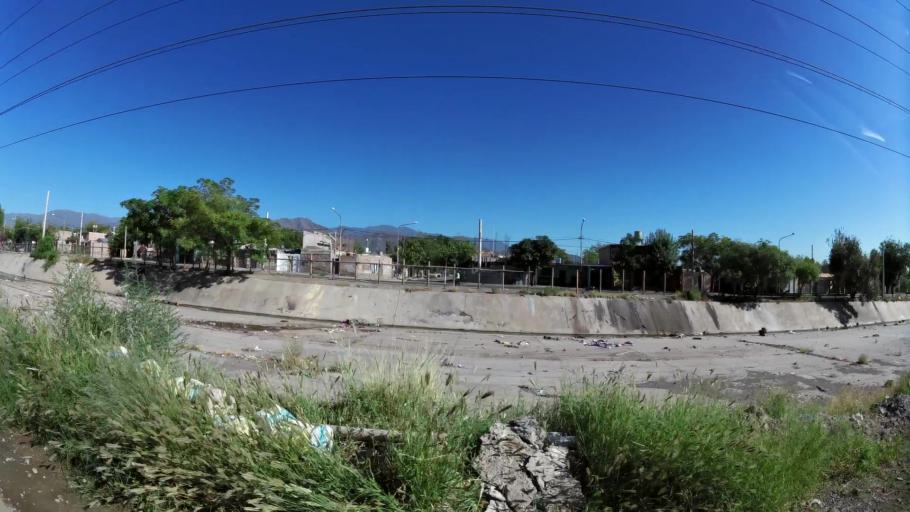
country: AR
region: Mendoza
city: Las Heras
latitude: -32.8698
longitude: -68.8621
